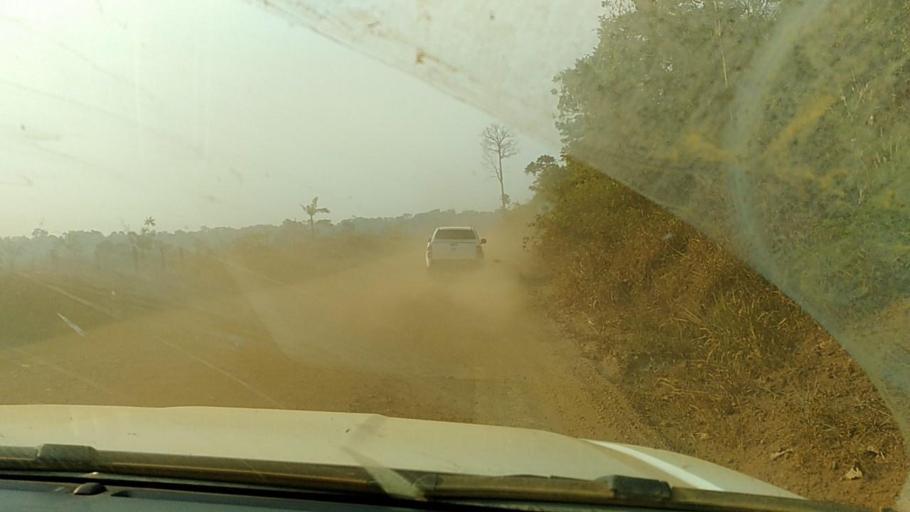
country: BR
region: Rondonia
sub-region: Porto Velho
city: Porto Velho
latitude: -8.7430
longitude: -63.9648
